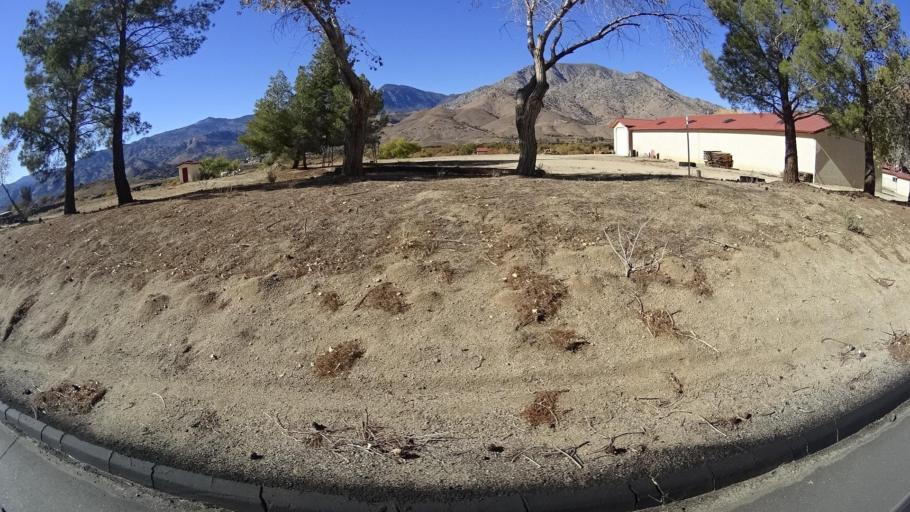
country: US
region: California
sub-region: Kern County
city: Wofford Heights
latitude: 35.7084
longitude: -118.4216
